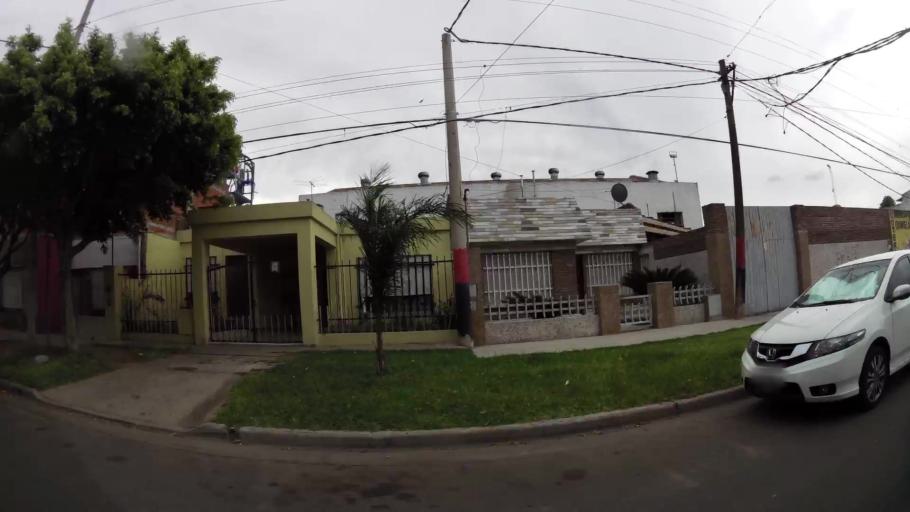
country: AR
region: Santa Fe
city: Gobernador Galvez
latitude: -32.9942
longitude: -60.6682
